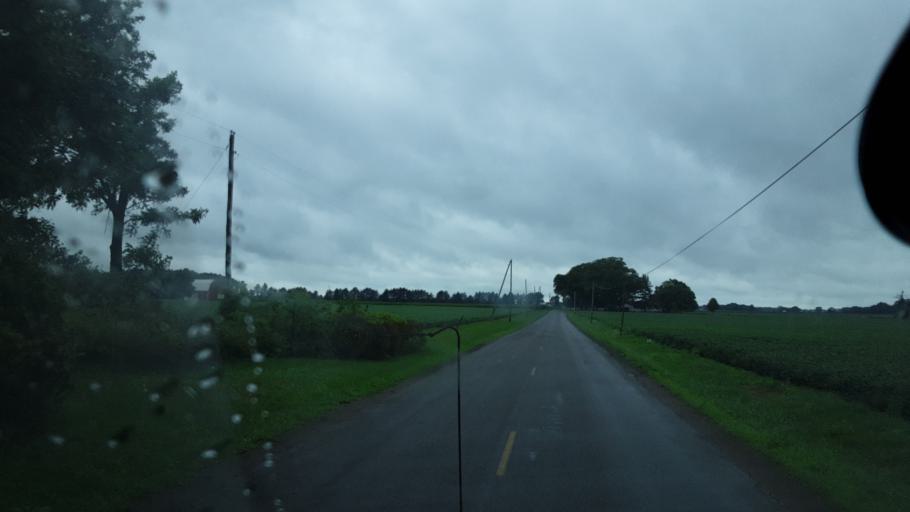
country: US
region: Ohio
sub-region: Van Wert County
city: Van Wert
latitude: 40.8004
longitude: -84.6252
